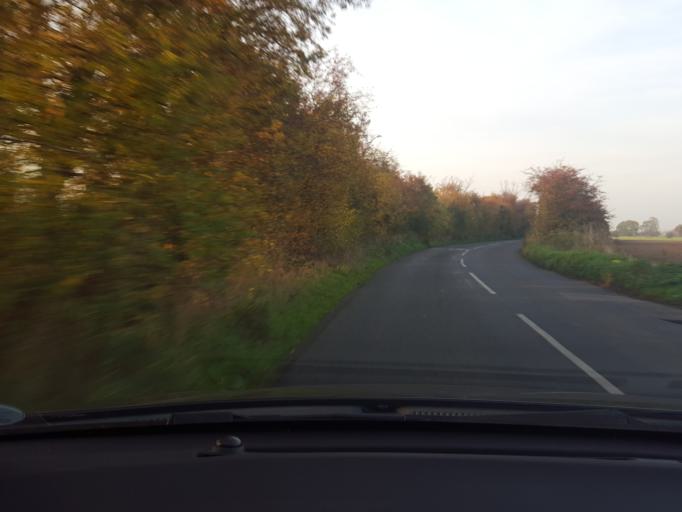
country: GB
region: England
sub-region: Essex
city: Saint Osyth
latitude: 51.7874
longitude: 1.0869
